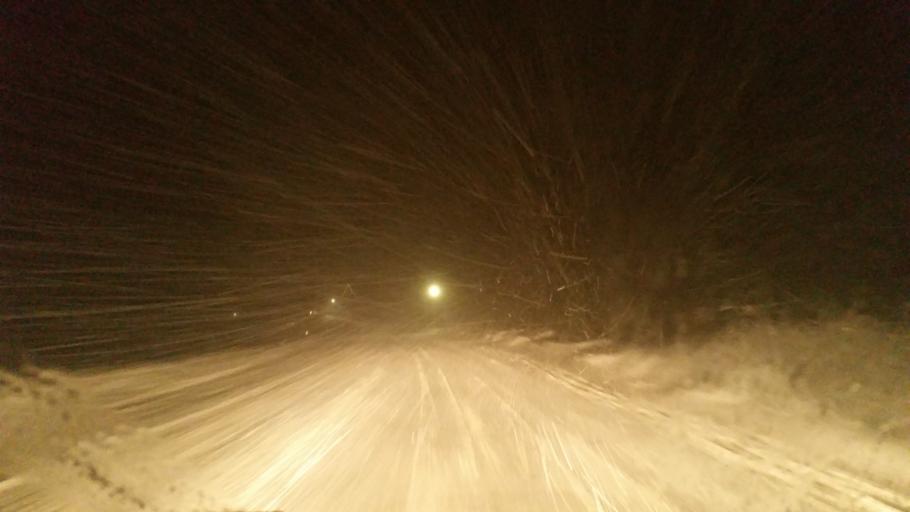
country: AT
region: Salzburg
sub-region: Politischer Bezirk Hallein
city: Abtenau
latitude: 47.5214
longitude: 13.4311
